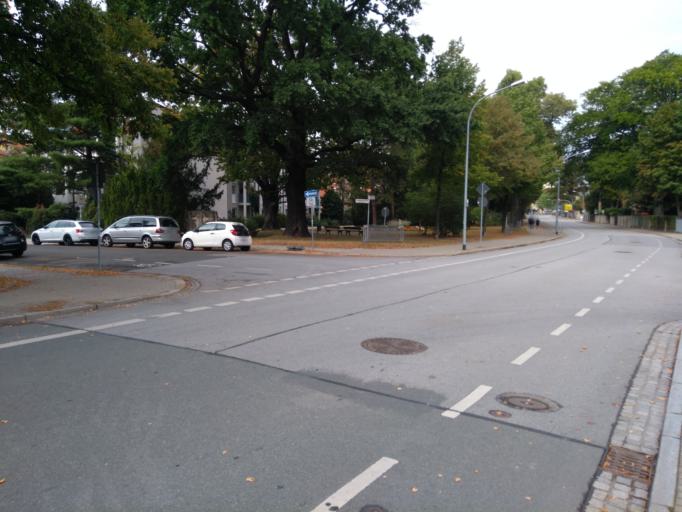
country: DE
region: Saxony
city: Bautzen
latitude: 51.1786
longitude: 14.4327
